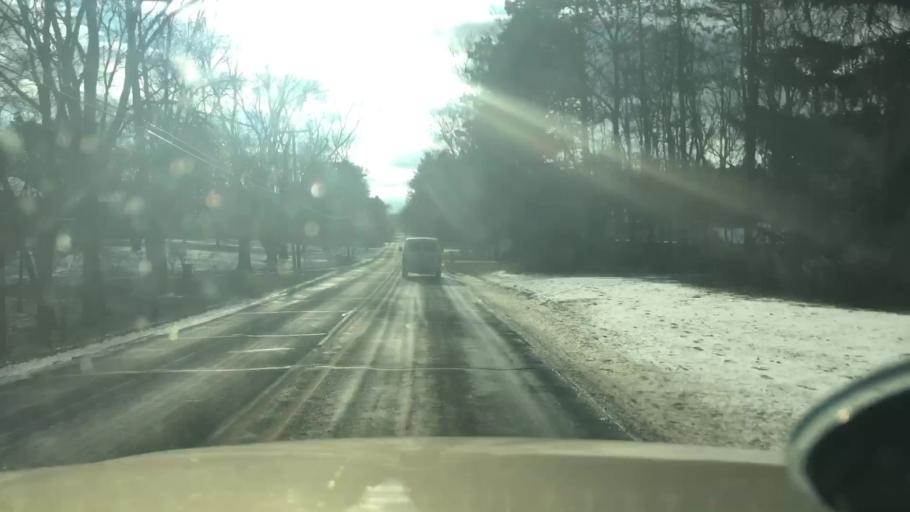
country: US
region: Michigan
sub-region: Jackson County
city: Vandercook Lake
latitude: 42.1980
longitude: -84.4431
